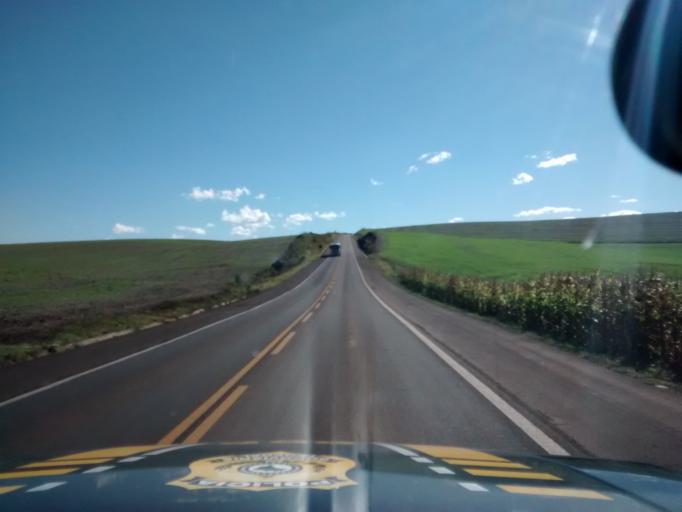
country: BR
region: Rio Grande do Sul
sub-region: Lagoa Vermelha
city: Lagoa Vermelha
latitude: -28.3176
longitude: -51.3519
